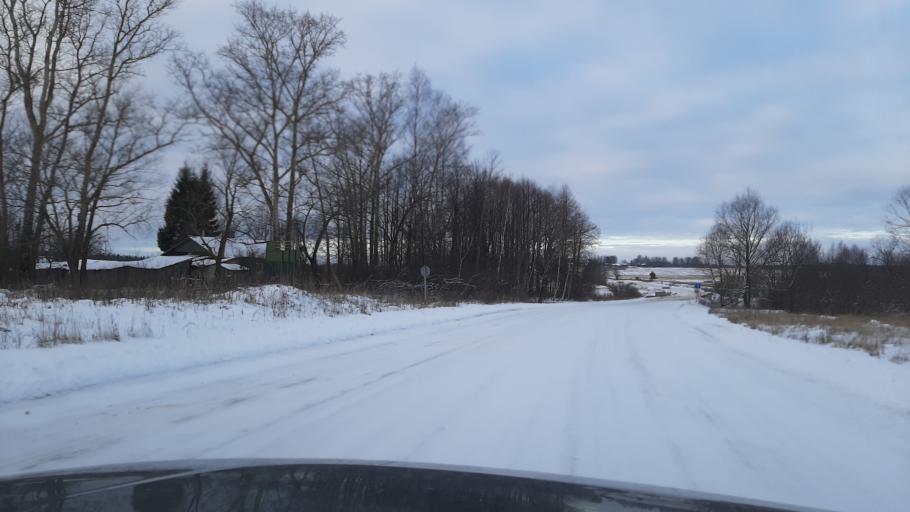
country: RU
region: Kostroma
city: Kosmynino
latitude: 57.4819
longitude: 40.7946
